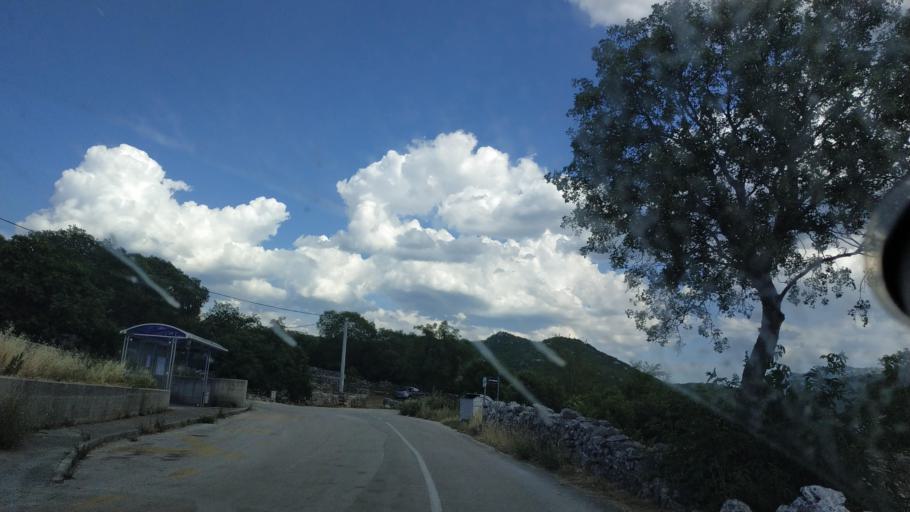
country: HR
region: Splitsko-Dalmatinska
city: Dugopolje
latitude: 43.5638
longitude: 16.6539
